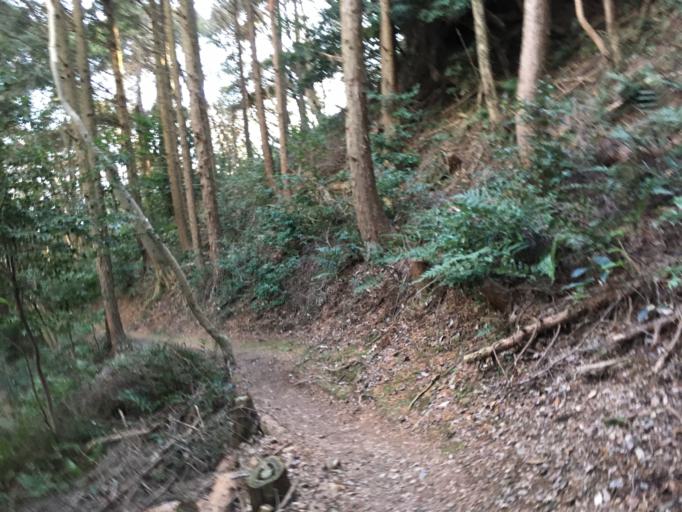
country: JP
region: Aichi
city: Toyohashi
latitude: 34.7401
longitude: 137.4533
